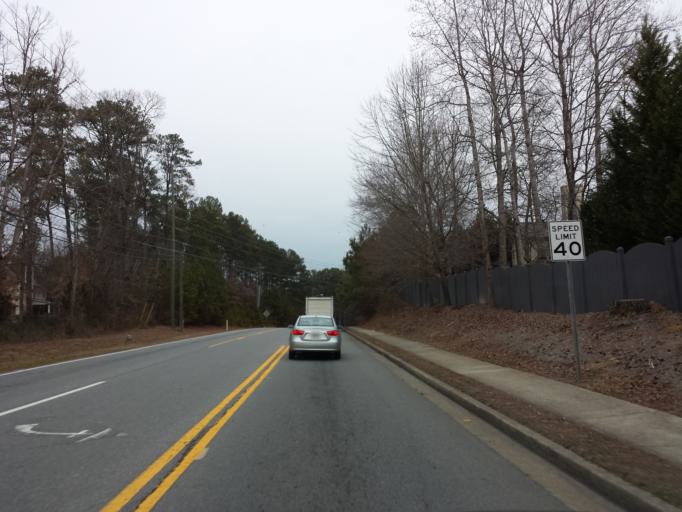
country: US
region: Georgia
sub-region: Cobb County
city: Marietta
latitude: 33.9854
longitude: -84.5124
